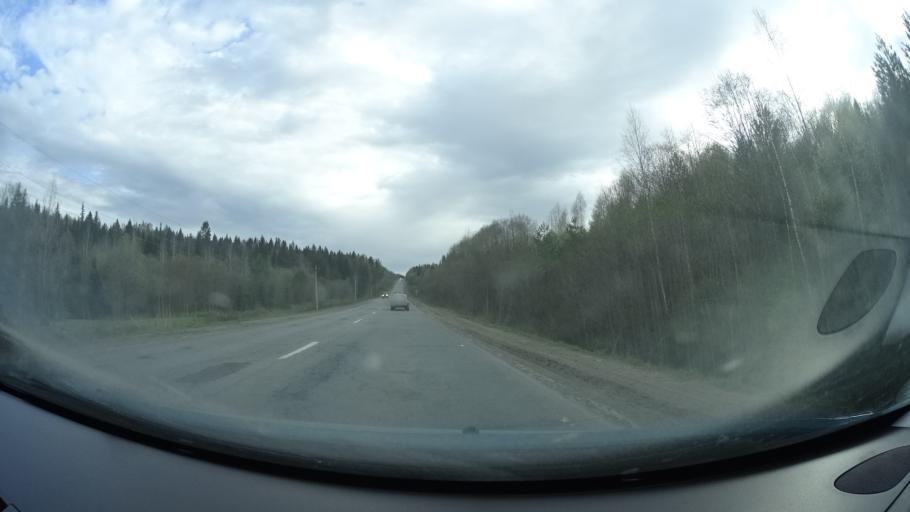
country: RU
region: Perm
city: Kultayevo
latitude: 57.8005
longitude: 55.7814
